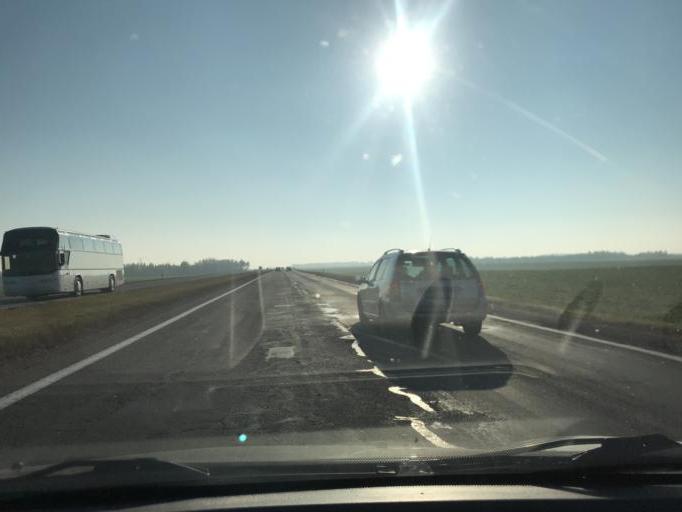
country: BY
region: Minsk
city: Dukora
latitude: 53.6483
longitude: 27.9785
